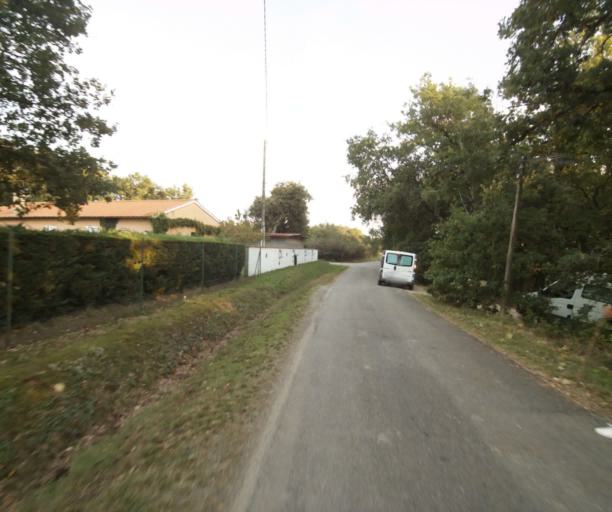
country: FR
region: Midi-Pyrenees
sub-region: Departement du Tarn-et-Garonne
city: Pompignan
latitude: 43.8264
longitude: 1.3134
